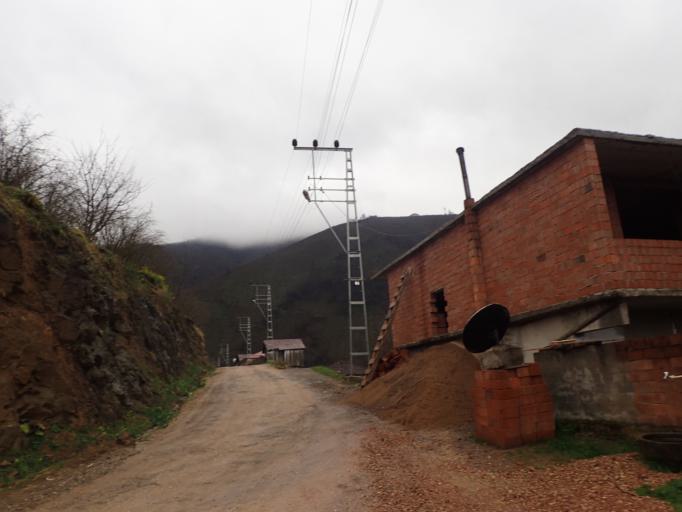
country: TR
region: Ordu
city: Camas
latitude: 40.8723
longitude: 37.5082
